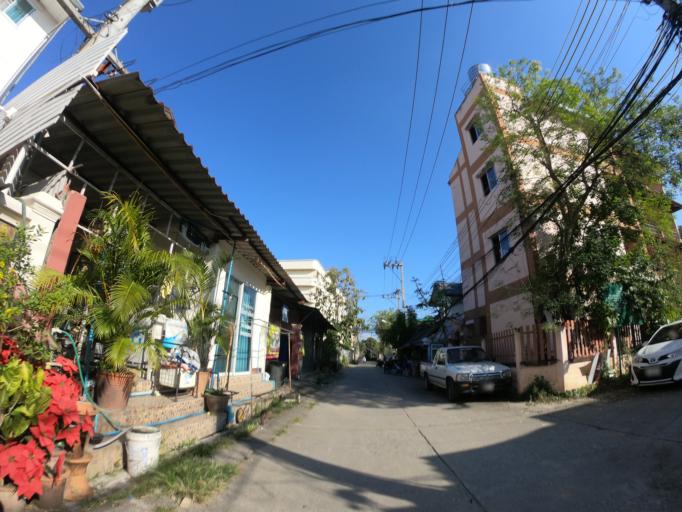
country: TH
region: Chiang Mai
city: Chiang Mai
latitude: 18.7621
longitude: 98.9789
